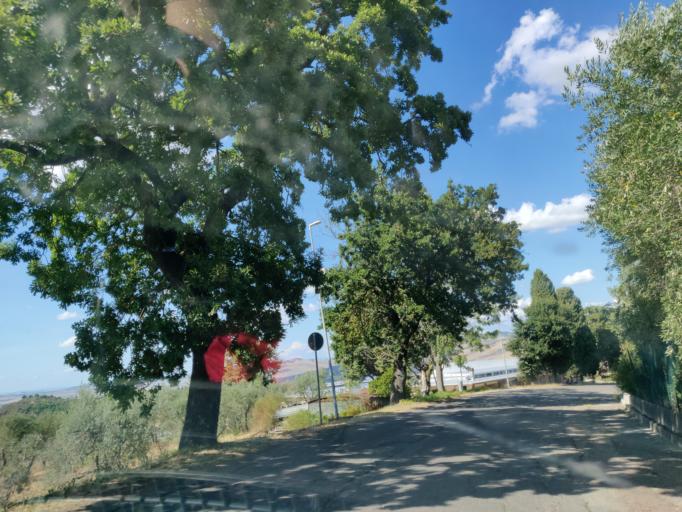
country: IT
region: Tuscany
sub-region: Provincia di Siena
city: Radicofani
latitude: 42.9767
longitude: 11.7391
